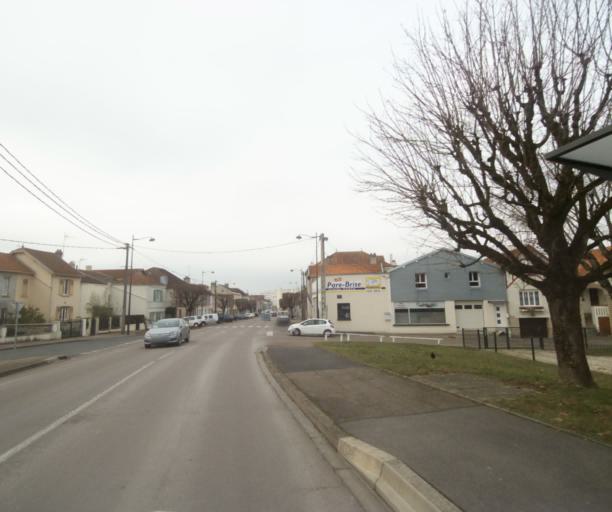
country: FR
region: Champagne-Ardenne
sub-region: Departement de la Haute-Marne
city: Saint-Dizier
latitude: 48.6358
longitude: 4.9631
